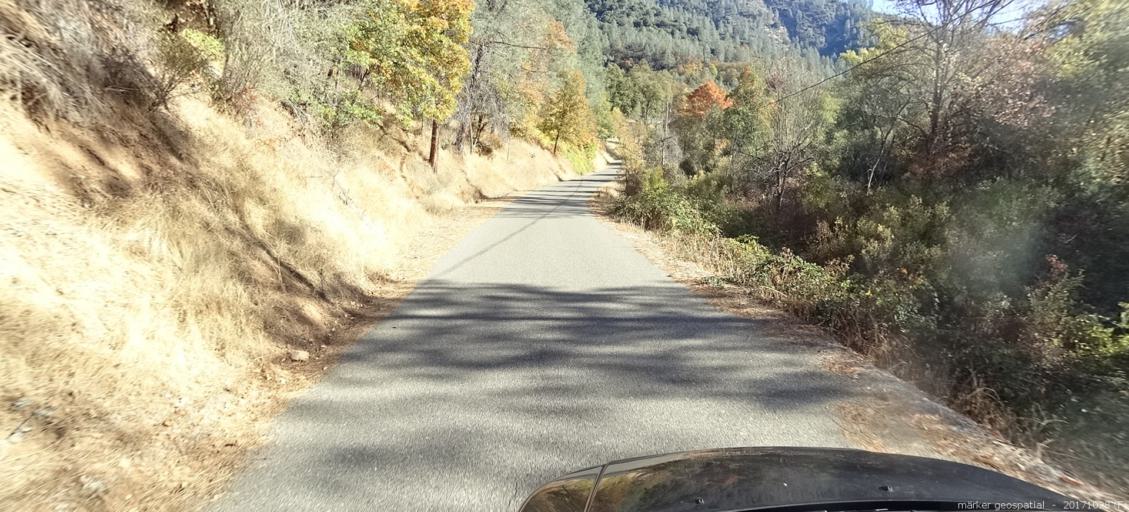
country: US
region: California
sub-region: Shasta County
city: Shasta
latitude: 40.7594
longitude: -122.6056
